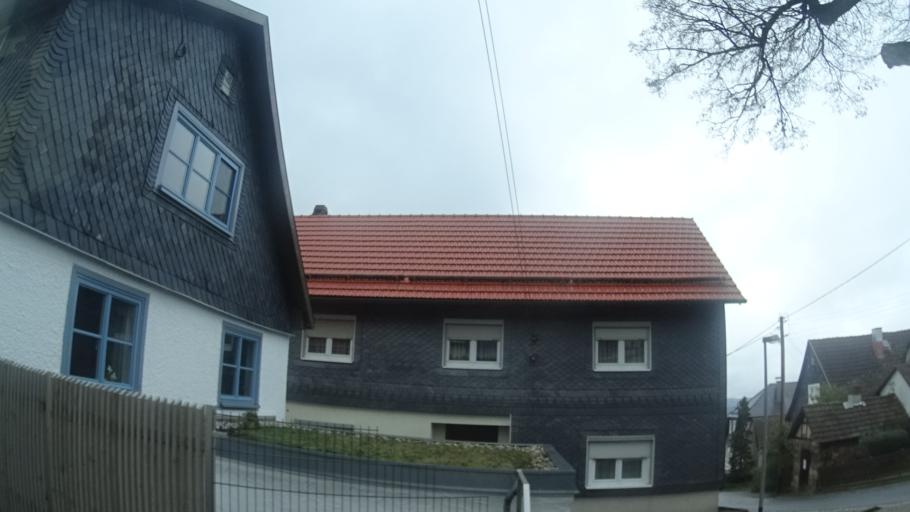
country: DE
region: Thuringia
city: Eisfeld
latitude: 50.4873
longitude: 10.8514
